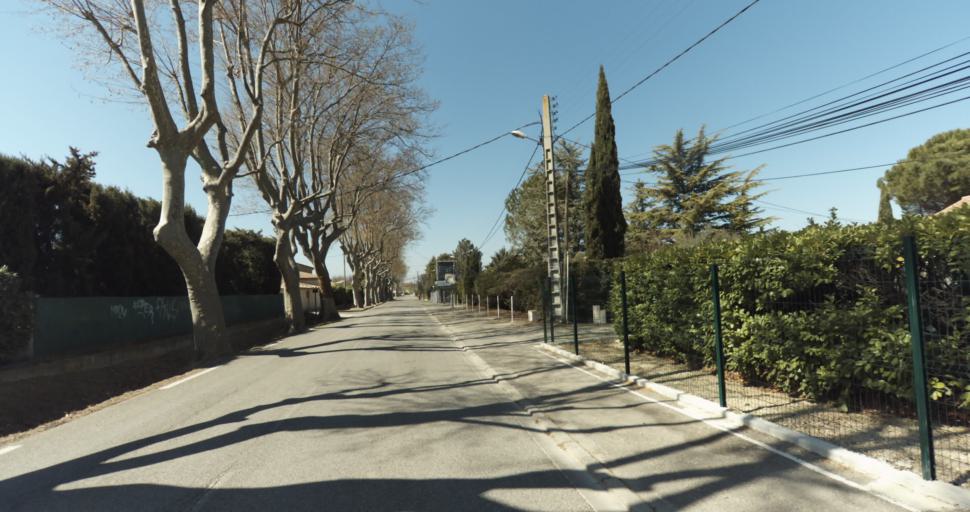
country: FR
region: Provence-Alpes-Cote d'Azur
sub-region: Departement des Bouches-du-Rhone
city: Pelissanne
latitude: 43.6286
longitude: 5.1598
